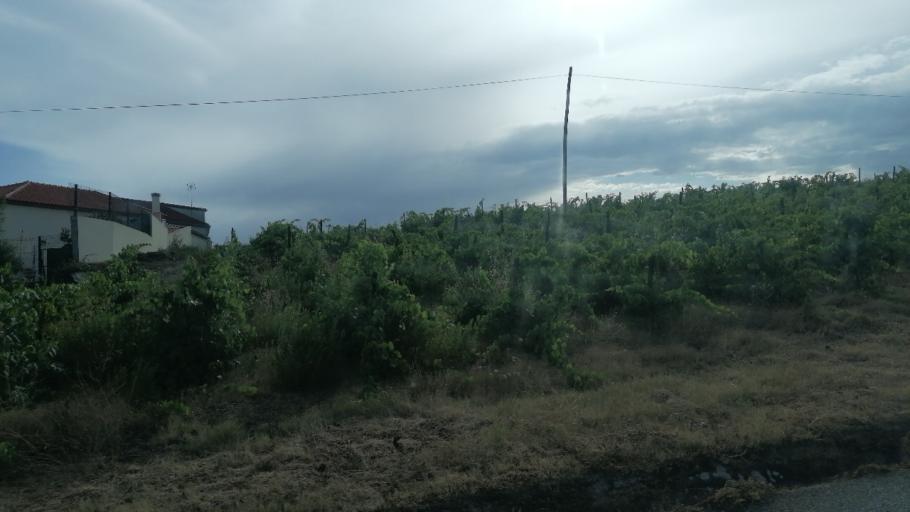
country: PT
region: Viseu
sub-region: Sao Joao da Pesqueira
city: Sao Joao da Pesqueira
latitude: 41.1024
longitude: -7.3824
